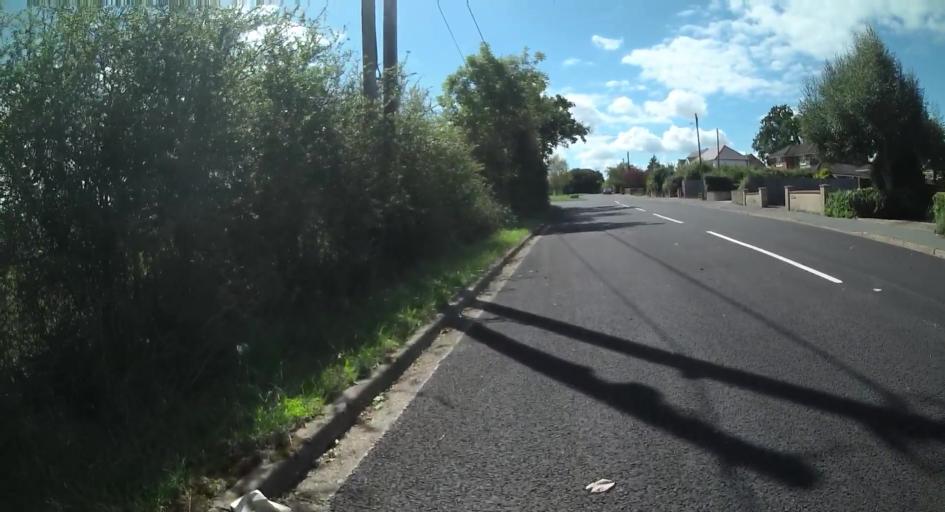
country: GB
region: England
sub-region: Isle of Wight
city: Newport
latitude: 50.7228
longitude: -1.2675
